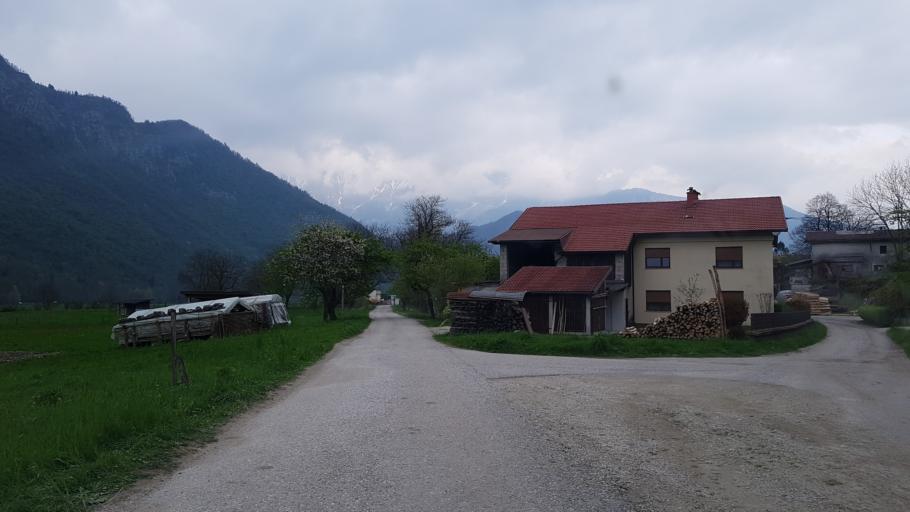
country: SI
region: Kobarid
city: Kobarid
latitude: 46.2425
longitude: 13.5489
